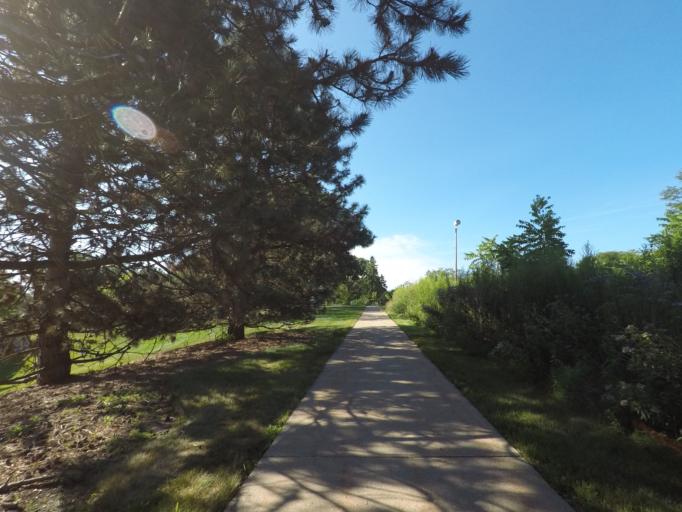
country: US
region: Wisconsin
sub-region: Dane County
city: Shorewood Hills
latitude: 43.0543
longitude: -89.4686
